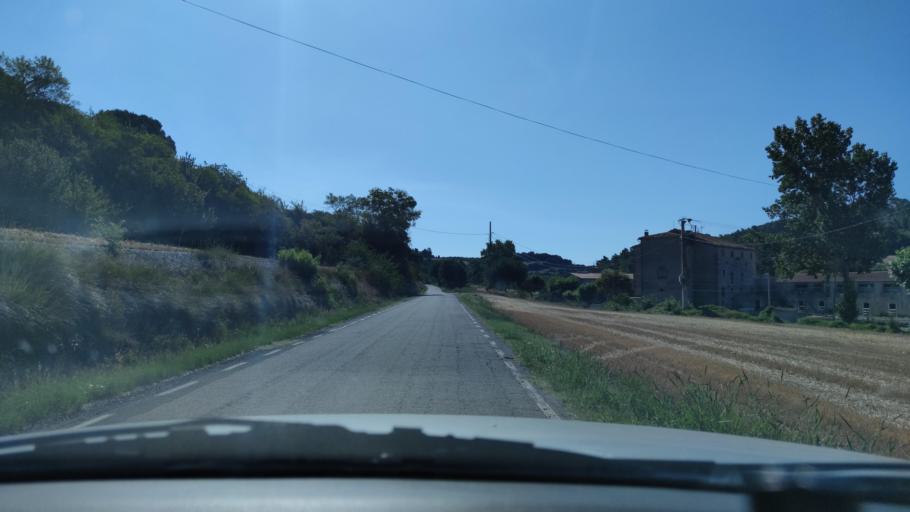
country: ES
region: Catalonia
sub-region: Provincia de Barcelona
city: Pujalt
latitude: 41.6877
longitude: 1.3899
